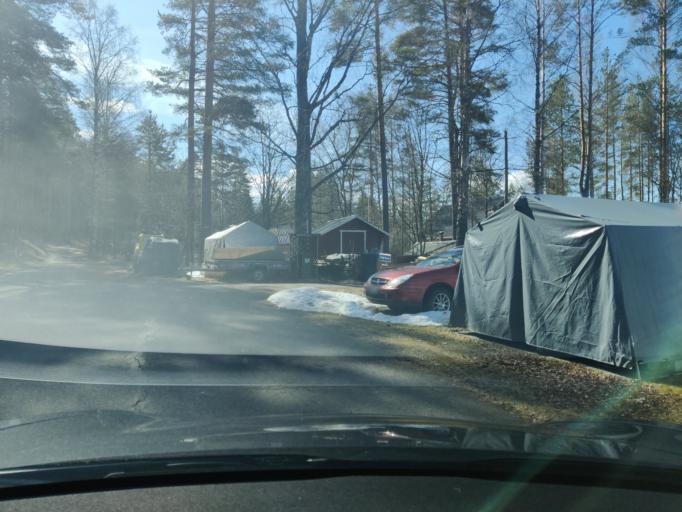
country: FI
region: Northern Savo
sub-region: Kuopio
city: Vehmersalmi
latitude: 62.7573
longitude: 28.0328
